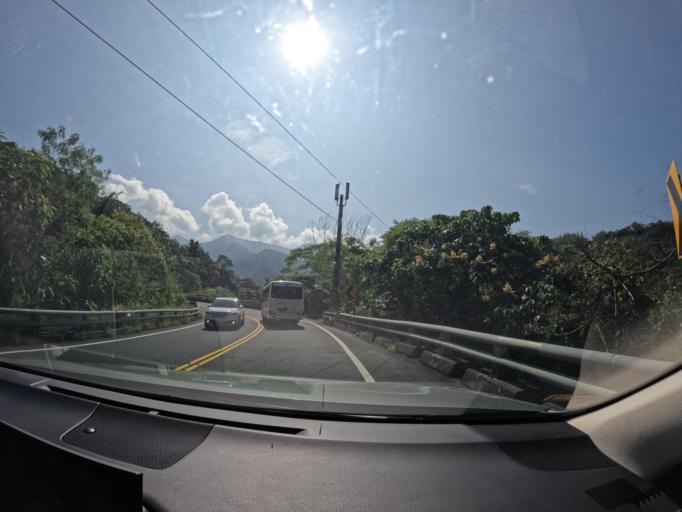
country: TW
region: Taiwan
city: Yujing
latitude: 23.0708
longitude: 120.6614
